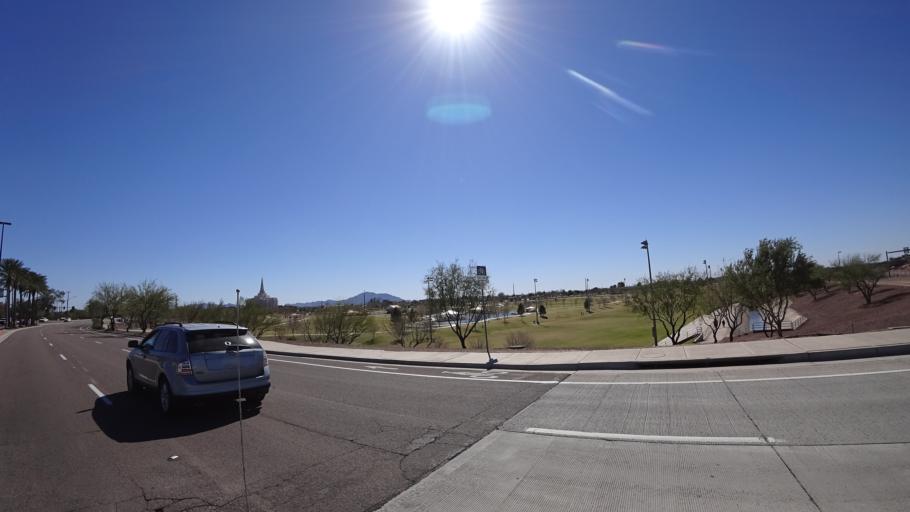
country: US
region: Arizona
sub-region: Maricopa County
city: Gilbert
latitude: 33.2967
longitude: -111.7410
